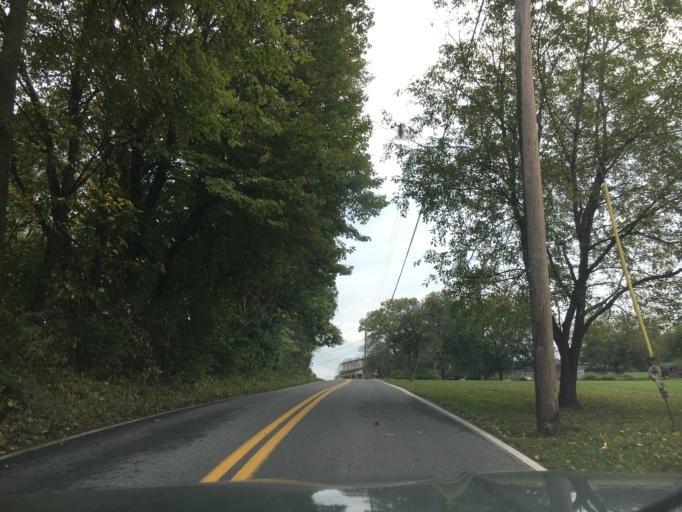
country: US
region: Pennsylvania
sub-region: Berks County
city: Fleetwood
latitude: 40.4539
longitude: -75.7588
